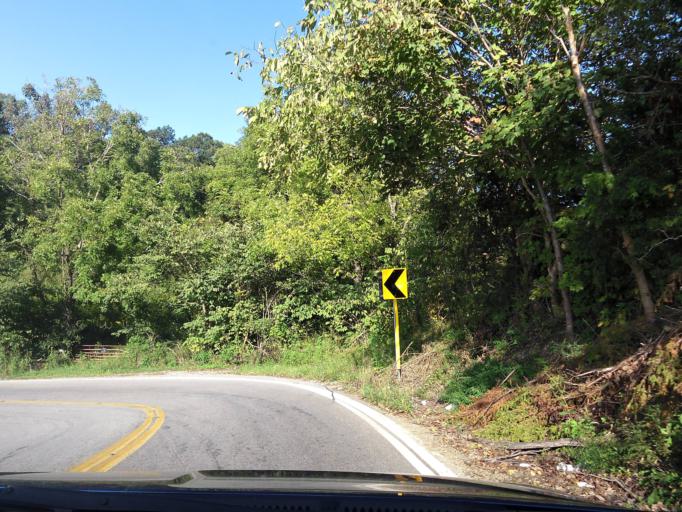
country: US
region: Tennessee
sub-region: Union County
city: Luttrell
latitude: 36.2314
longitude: -83.7420
